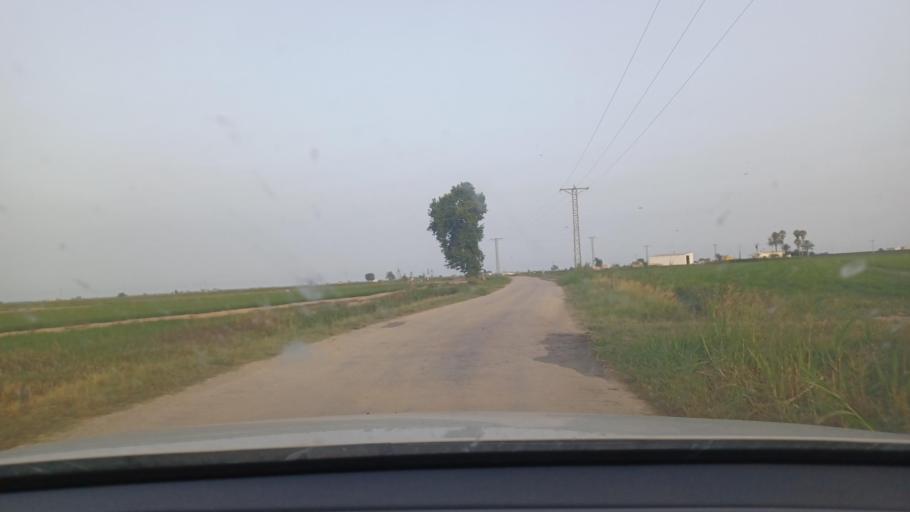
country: ES
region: Catalonia
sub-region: Provincia de Tarragona
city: Amposta
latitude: 40.7034
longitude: 0.6369
